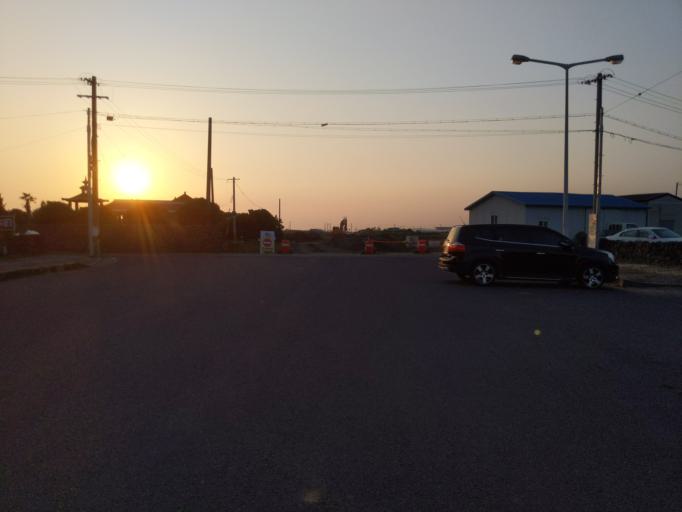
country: KR
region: Jeju-do
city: Gaigeturi
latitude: 33.2213
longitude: 126.2470
